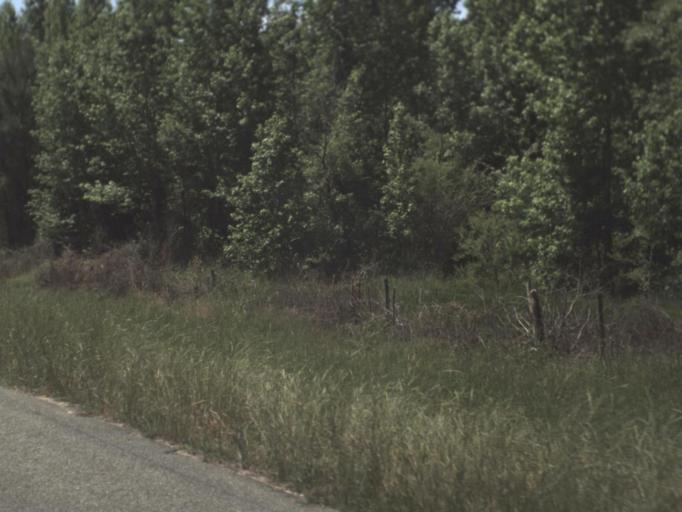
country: US
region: Florida
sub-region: Jackson County
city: Marianna
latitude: 30.6576
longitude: -85.2177
